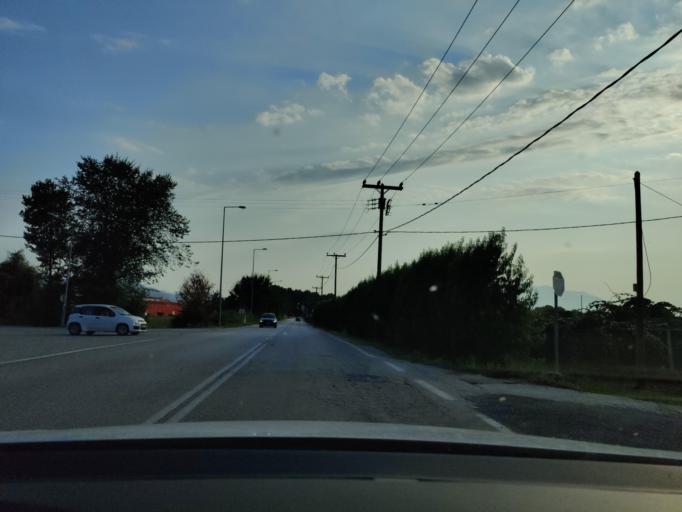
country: GR
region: East Macedonia and Thrace
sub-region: Nomos Kavalas
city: Amygdaleonas
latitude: 40.9727
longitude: 24.3557
